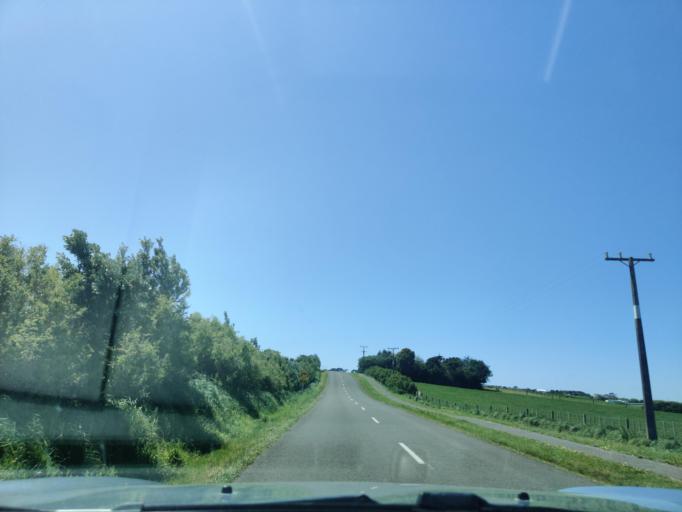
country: NZ
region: Taranaki
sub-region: South Taranaki District
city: Hawera
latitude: -39.6020
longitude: 174.2481
